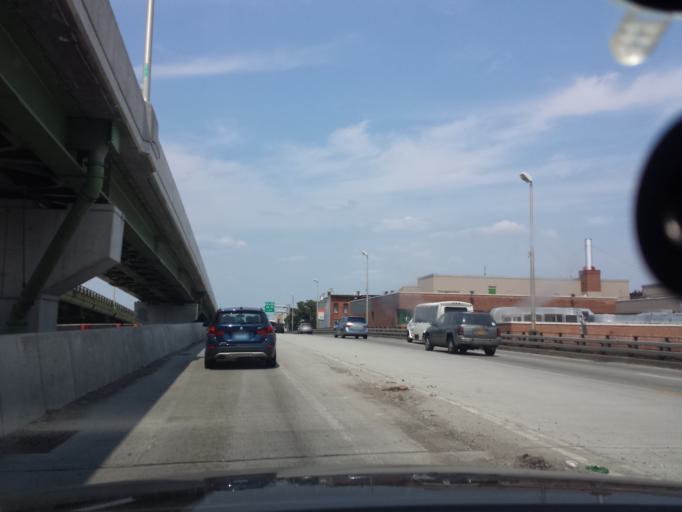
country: US
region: New York
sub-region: Kings County
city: Bensonhurst
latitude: 40.6418
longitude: -74.0206
